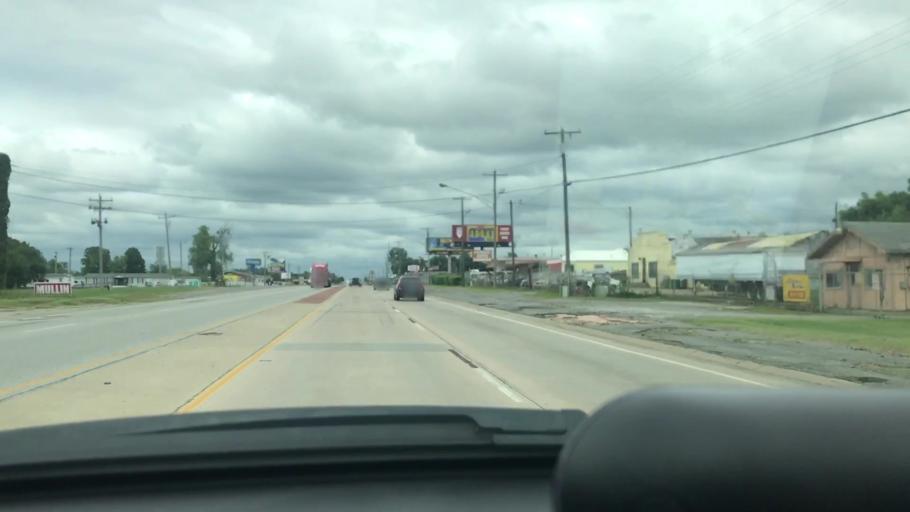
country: US
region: Oklahoma
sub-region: Muskogee County
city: Muskogee
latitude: 35.7727
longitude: -95.4025
